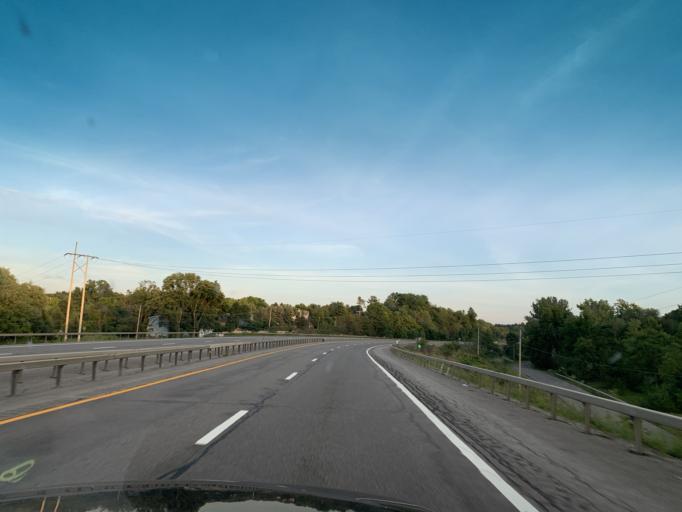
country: US
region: New York
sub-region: Oneida County
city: Washington Mills
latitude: 43.0419
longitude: -75.2732
